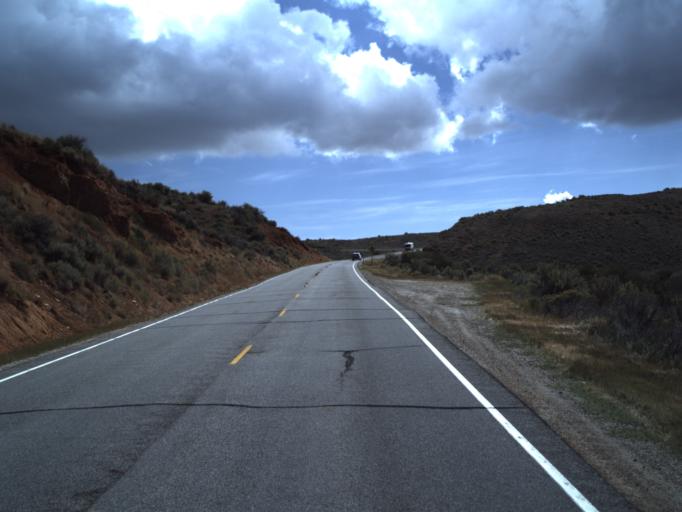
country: US
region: Utah
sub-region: Rich County
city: Randolph
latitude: 41.8117
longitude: -111.2641
